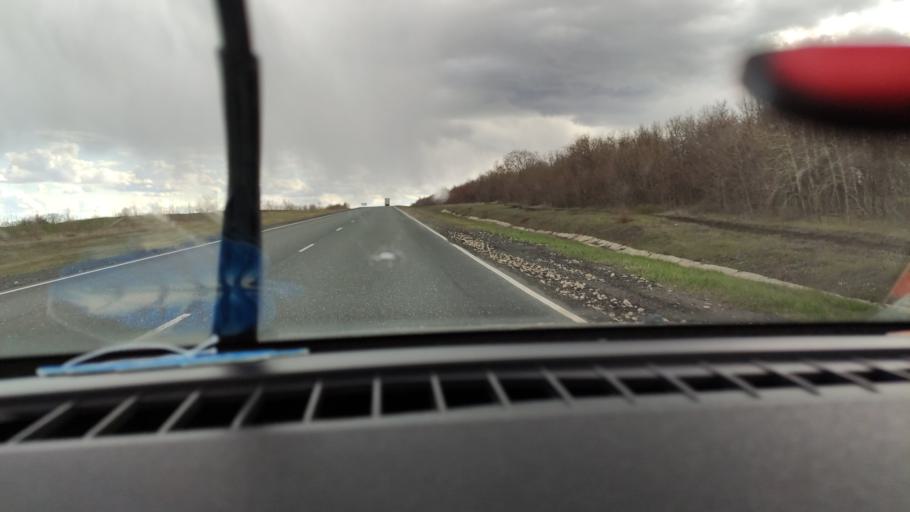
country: RU
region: Saratov
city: Balakovo
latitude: 52.1822
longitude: 47.8433
